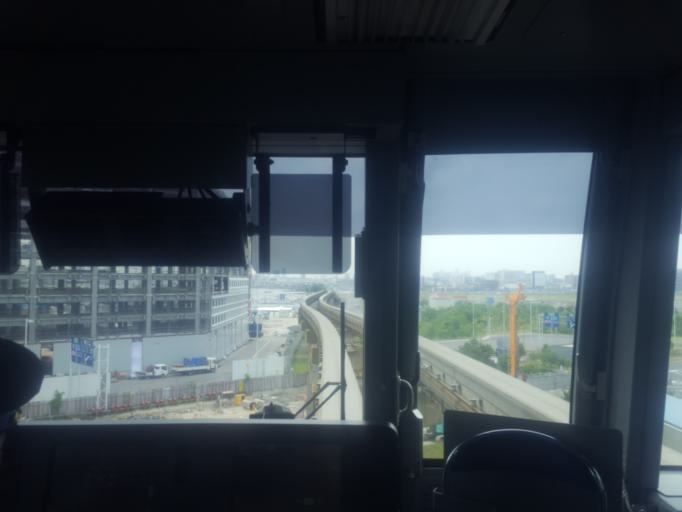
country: JP
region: Kanagawa
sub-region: Kawasaki-shi
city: Kawasaki
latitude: 35.5448
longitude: 139.7668
